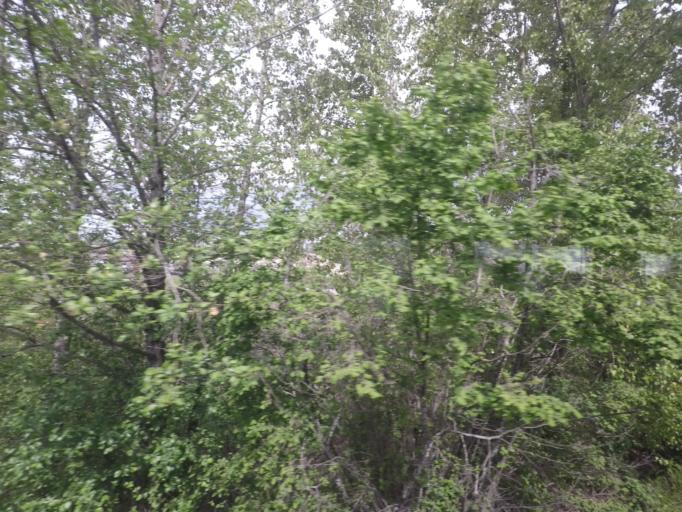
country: CA
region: British Columbia
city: New Westminster
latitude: 49.1997
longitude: -122.8907
